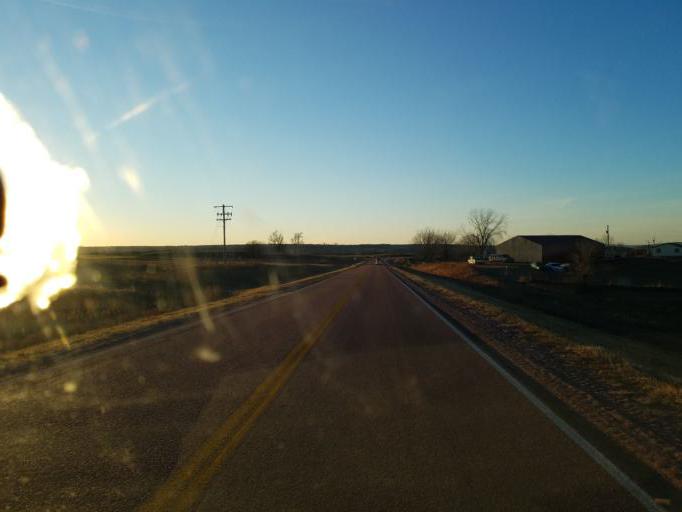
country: US
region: South Dakota
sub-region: Bon Homme County
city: Springfield
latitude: 42.7333
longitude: -97.8905
